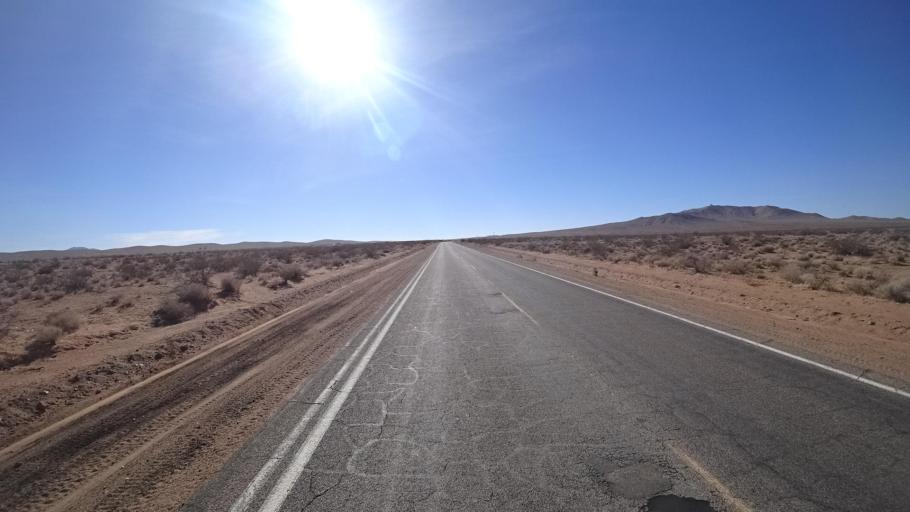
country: US
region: California
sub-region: Kern County
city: Ridgecrest
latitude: 35.4899
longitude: -117.6319
